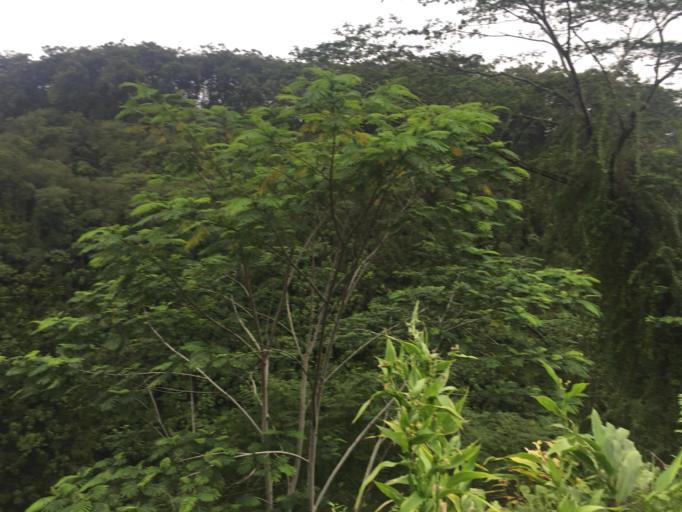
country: US
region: Hawaii
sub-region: Hawaii County
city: Pepeekeo
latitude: 19.8539
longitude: -155.1541
